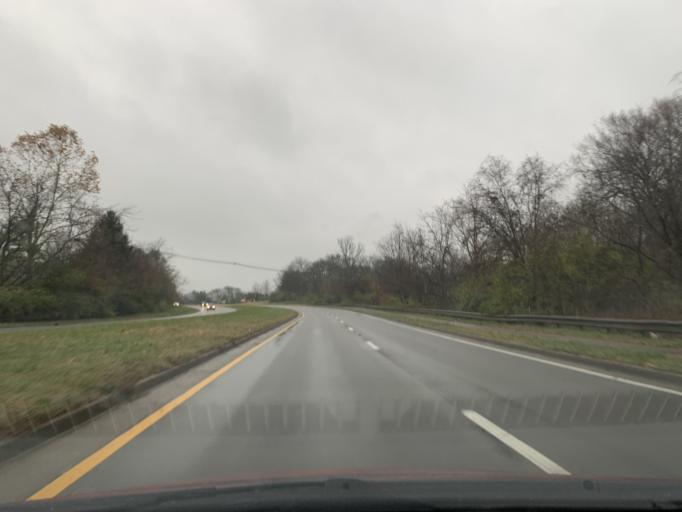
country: US
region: Kentucky
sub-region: Jefferson County
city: Hurstbourne Acres
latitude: 38.2053
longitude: -85.6026
